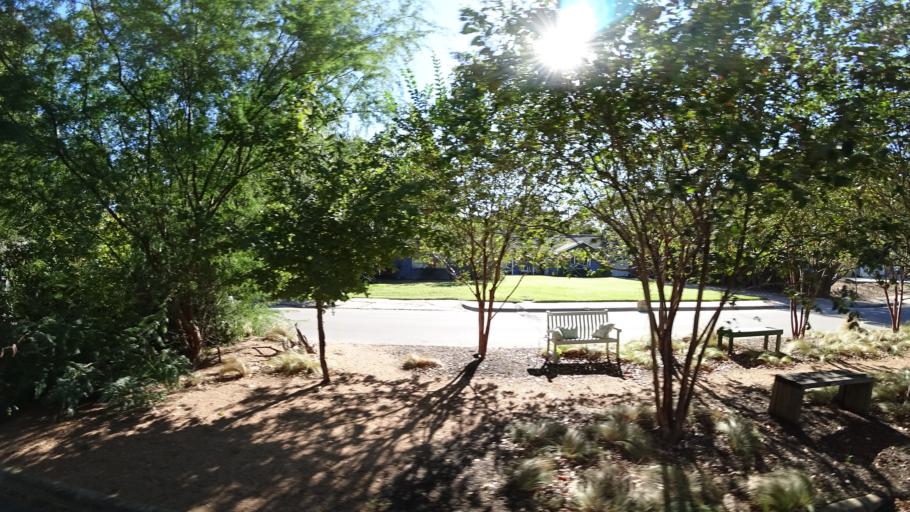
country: US
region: Texas
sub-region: Travis County
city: West Lake Hills
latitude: 30.3294
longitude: -97.7590
